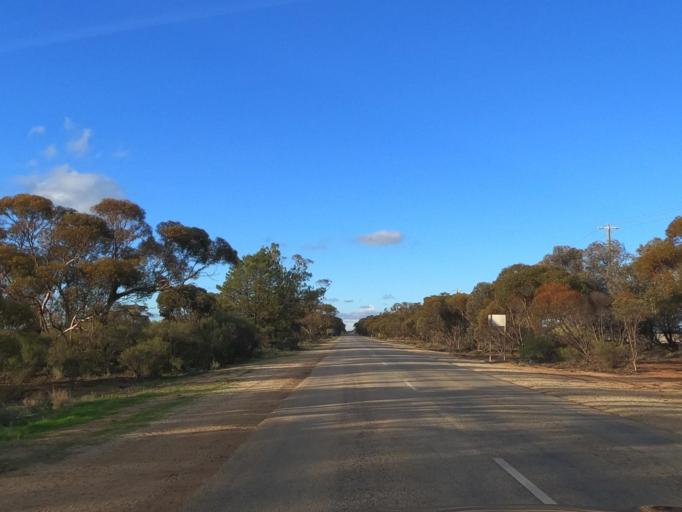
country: AU
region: Victoria
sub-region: Swan Hill
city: Swan Hill
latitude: -35.3480
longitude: 143.5165
